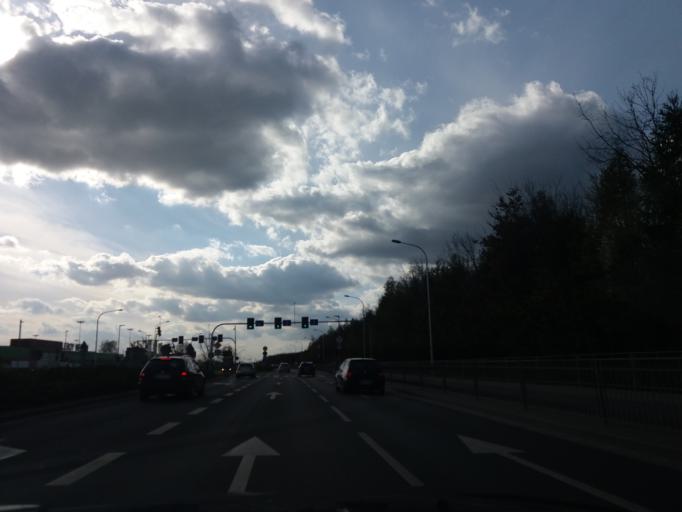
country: PL
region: Lower Silesian Voivodeship
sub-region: Powiat wroclawski
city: Smolec
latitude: 51.1084
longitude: 16.9468
